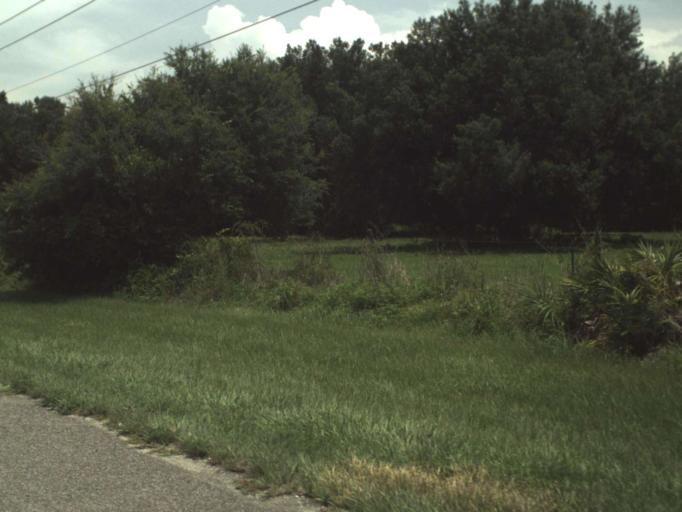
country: US
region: Florida
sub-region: Sumter County
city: Wildwood
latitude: 28.8324
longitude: -82.0455
